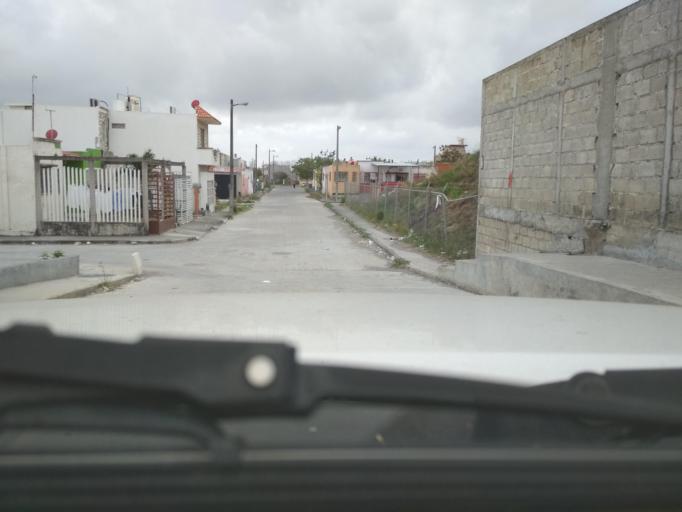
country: MX
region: Veracruz
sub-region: Veracruz
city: Oasis
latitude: 19.2074
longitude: -96.2266
